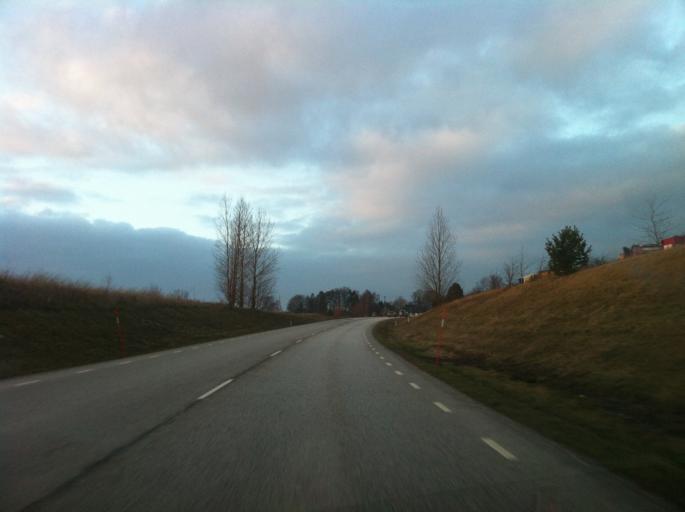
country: SE
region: Skane
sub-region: Kavlinge Kommun
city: Kaevlinge
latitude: 55.8169
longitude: 13.0908
